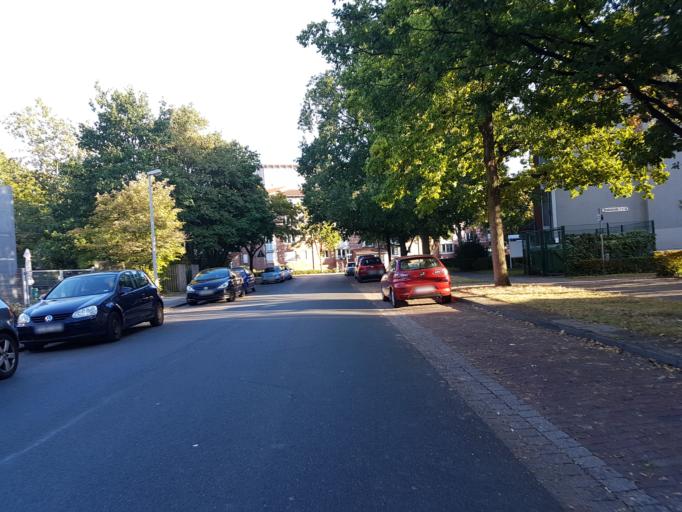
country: DE
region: Lower Saxony
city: Hannover
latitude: 52.4044
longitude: 9.7411
